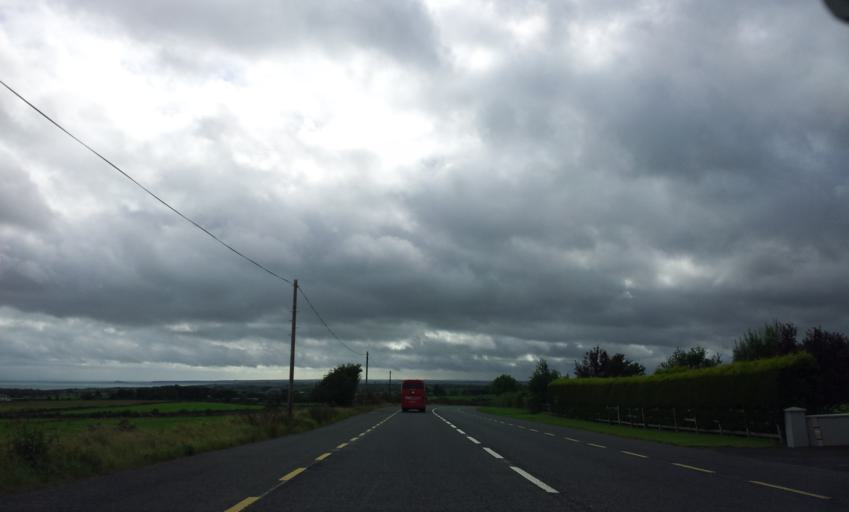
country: IE
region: Munster
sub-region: Waterford
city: Dungarvan
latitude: 52.0046
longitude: -7.7136
